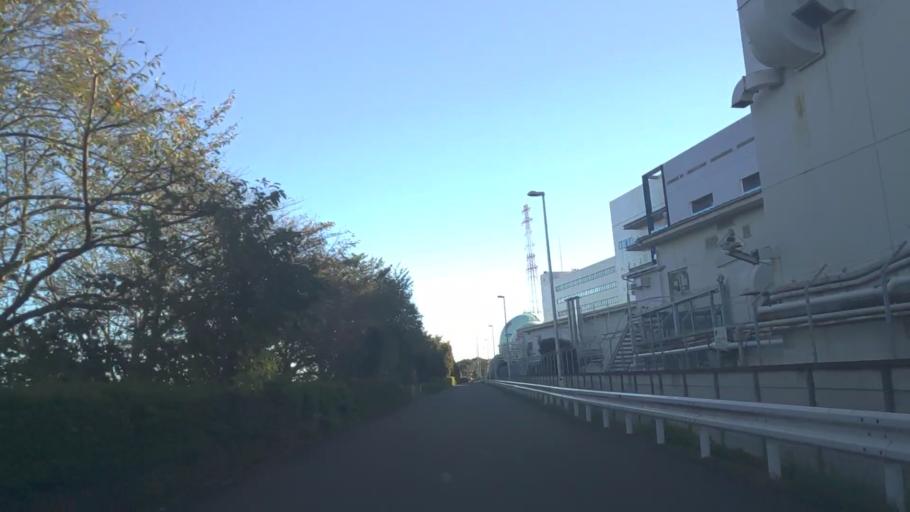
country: JP
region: Kanagawa
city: Atsugi
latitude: 35.4333
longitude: 139.3713
